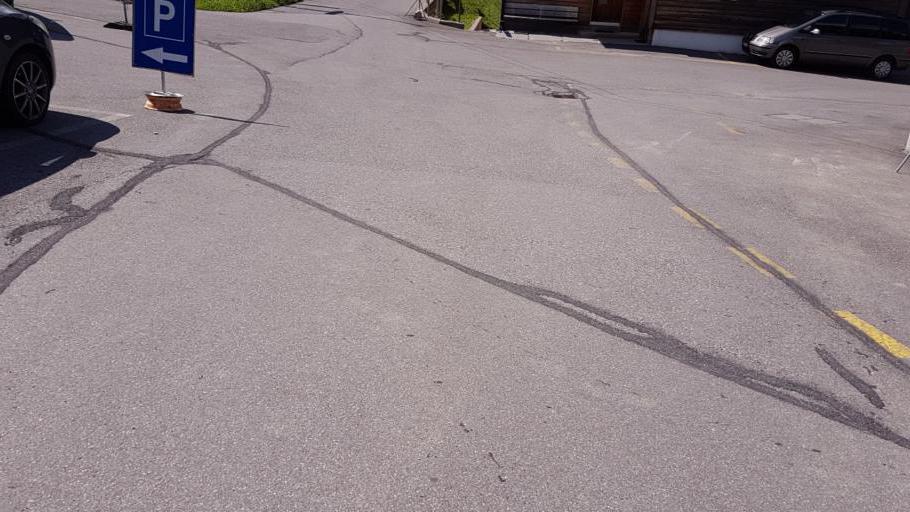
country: CH
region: Bern
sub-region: Frutigen-Niedersimmental District
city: Adelboden
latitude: 46.5293
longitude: 7.6064
